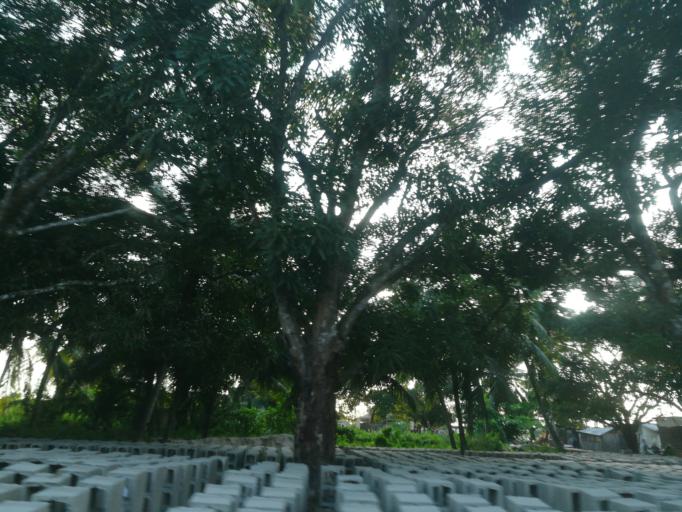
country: NG
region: Lagos
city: Badagry
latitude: 6.4708
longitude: 2.9928
